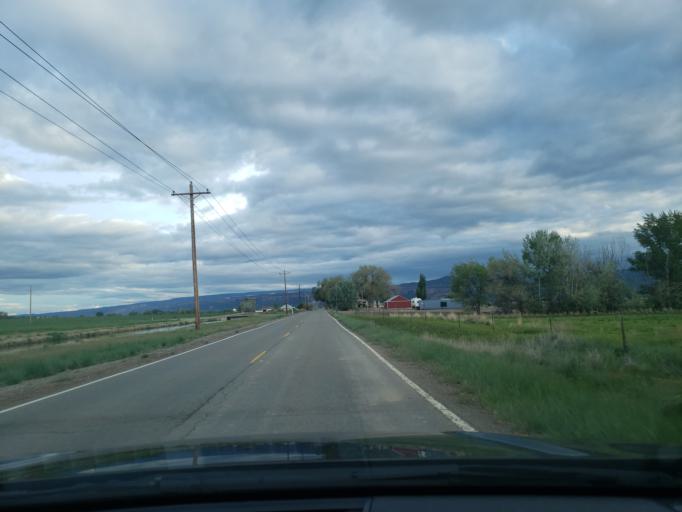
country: US
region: Colorado
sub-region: Mesa County
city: Fruita
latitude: 39.2001
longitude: -108.7012
